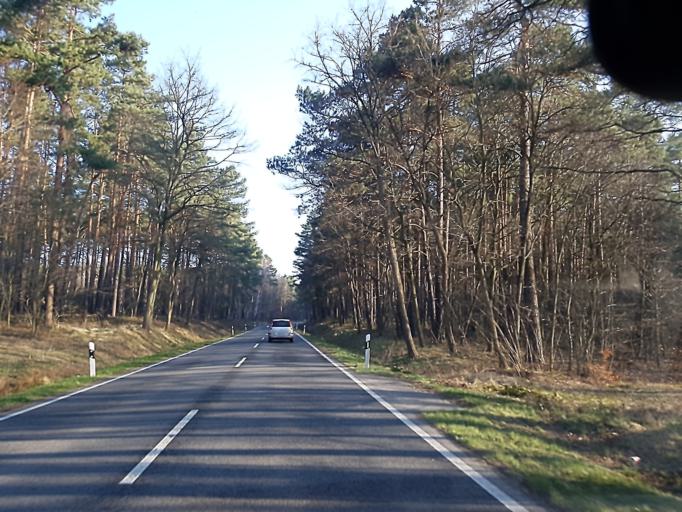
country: DE
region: Brandenburg
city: Bronkow
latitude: 51.7114
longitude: 13.9207
